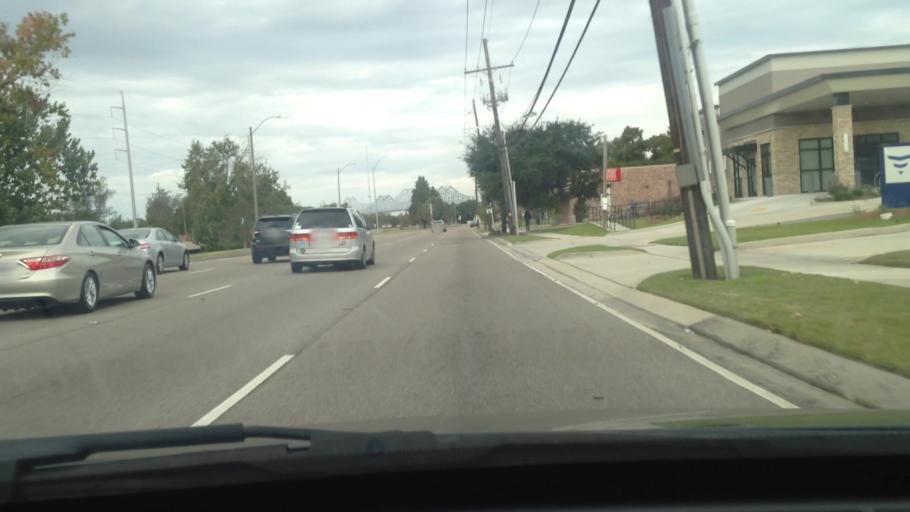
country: US
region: Louisiana
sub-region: Jefferson Parish
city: Terrytown
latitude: 29.9279
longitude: -90.0276
